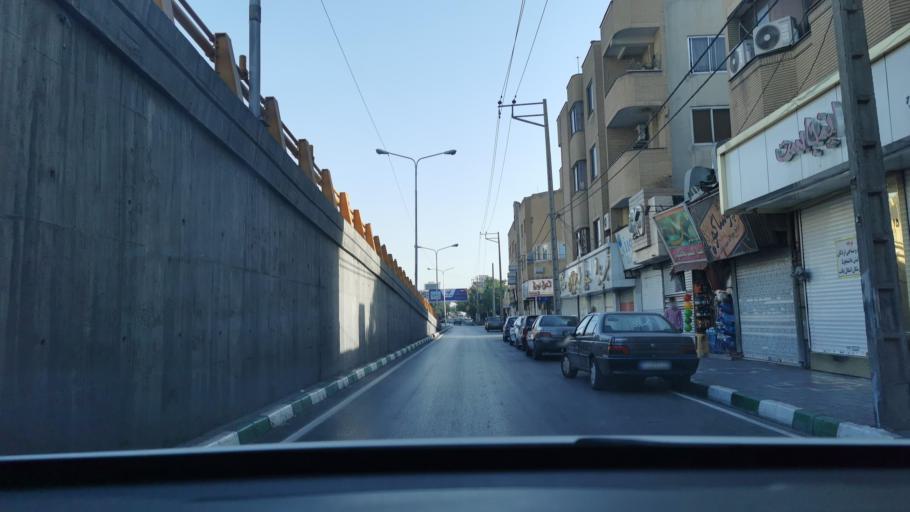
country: IR
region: Razavi Khorasan
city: Mashhad
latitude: 36.3285
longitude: 59.5021
